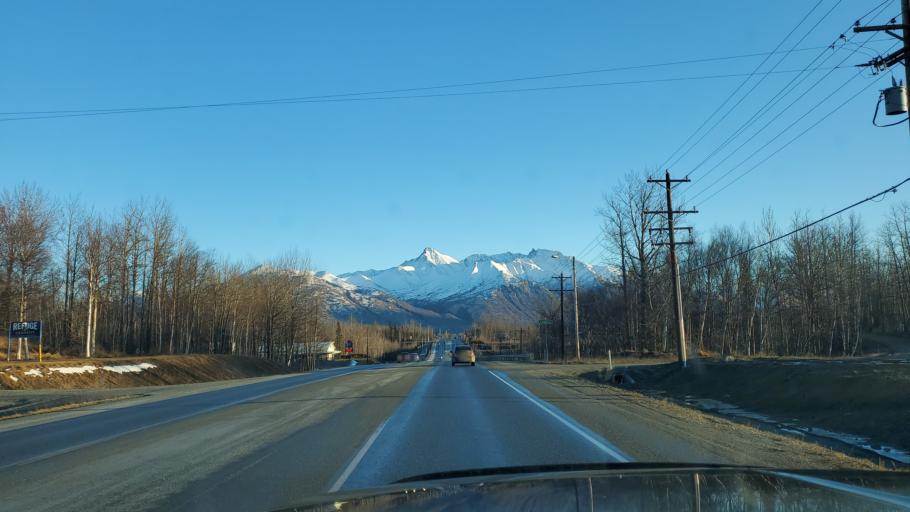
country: US
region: Alaska
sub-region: Matanuska-Susitna Borough
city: Palmer
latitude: 61.5995
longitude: -149.1459
